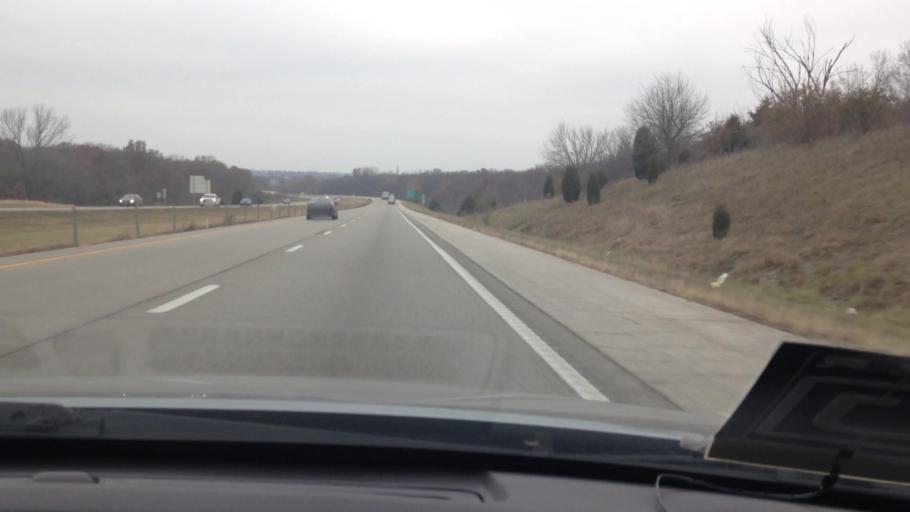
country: US
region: Missouri
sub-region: Cass County
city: Peculiar
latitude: 38.7524
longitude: -94.4799
